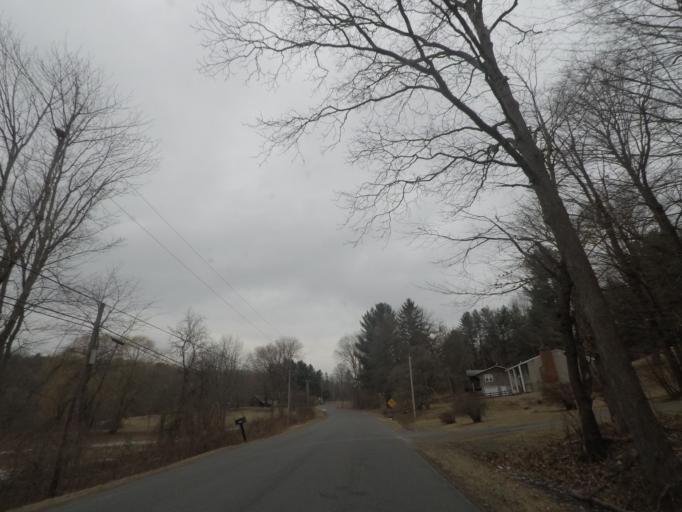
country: US
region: New York
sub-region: Rensselaer County
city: East Greenbush
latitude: 42.5640
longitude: -73.6576
